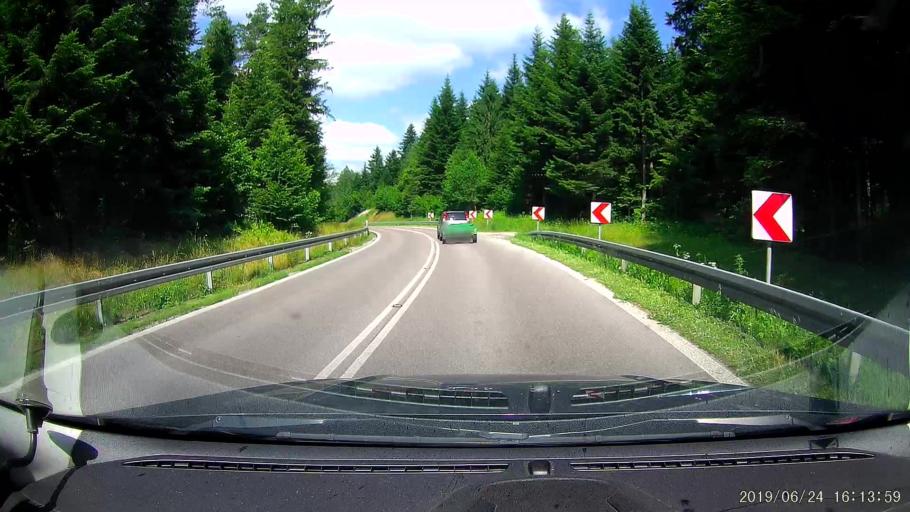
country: PL
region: Subcarpathian Voivodeship
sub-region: Powiat lubaczowski
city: Narol
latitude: 50.3736
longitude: 23.3773
